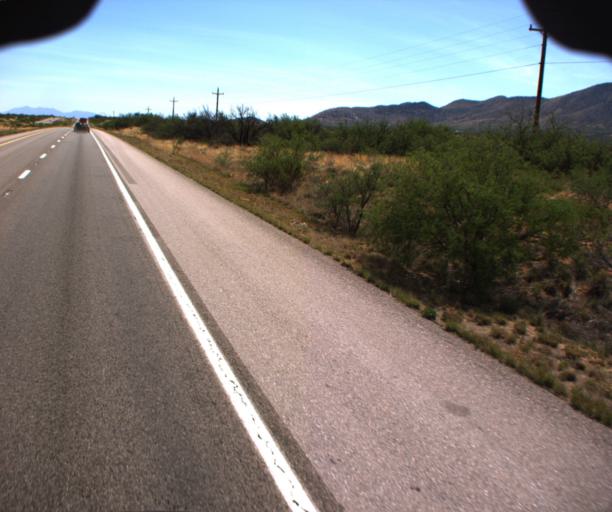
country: US
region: Arizona
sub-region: Cochise County
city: Whetstone
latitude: 31.8915
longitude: -110.3414
